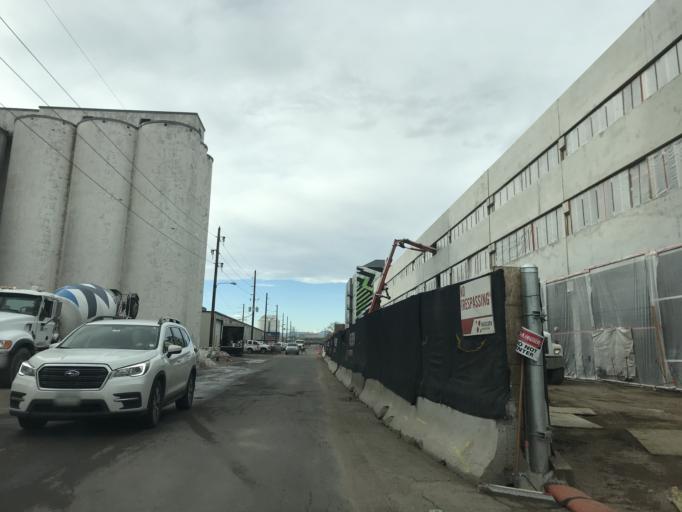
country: US
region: Colorado
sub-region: Denver County
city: Denver
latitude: 39.7719
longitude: -104.9752
